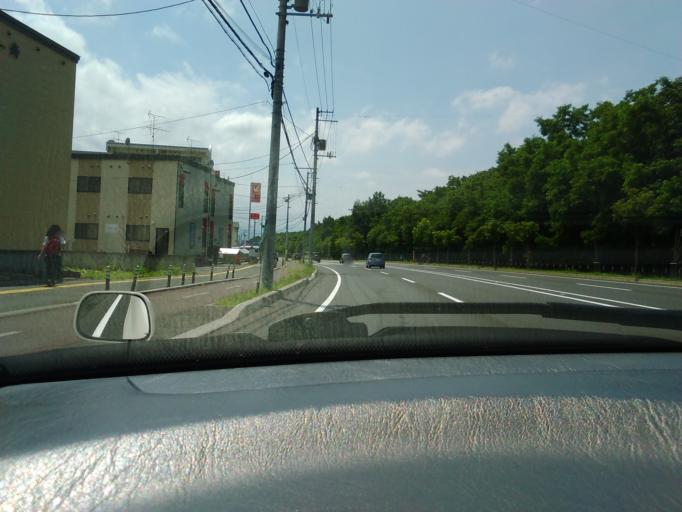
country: JP
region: Hokkaido
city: Ebetsu
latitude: 43.0700
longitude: 141.4930
